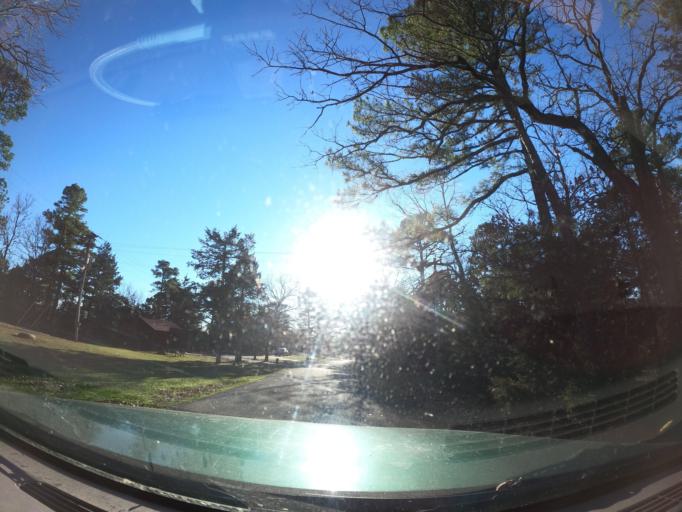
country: US
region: Oklahoma
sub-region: Latimer County
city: Wilburton
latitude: 34.9782
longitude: -95.3530
